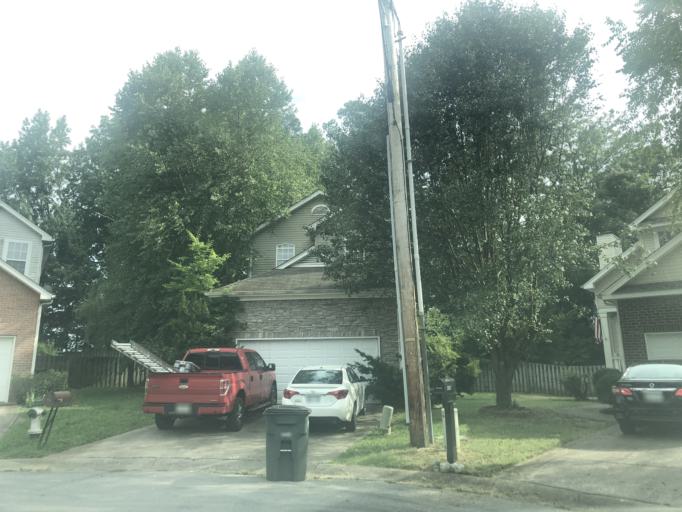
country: US
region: Tennessee
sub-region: Wilson County
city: Green Hill
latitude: 36.1845
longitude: -86.5841
